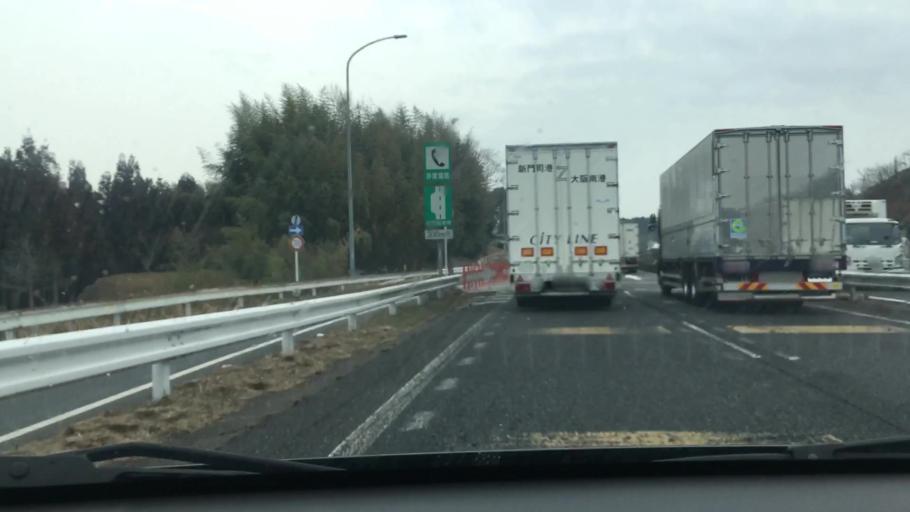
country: JP
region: Mie
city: Ueno-ebisumachi
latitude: 34.8192
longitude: 136.2174
